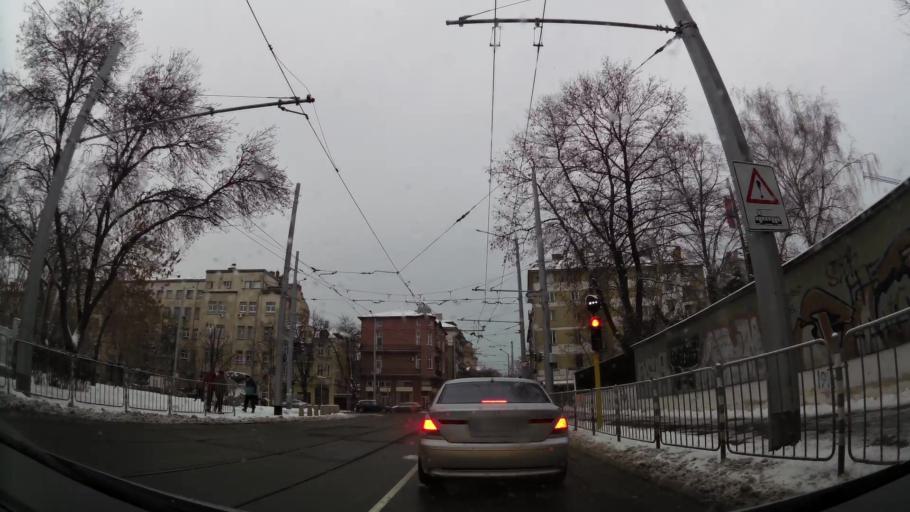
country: BG
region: Sofia-Capital
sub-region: Stolichna Obshtina
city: Sofia
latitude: 42.6971
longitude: 23.3378
